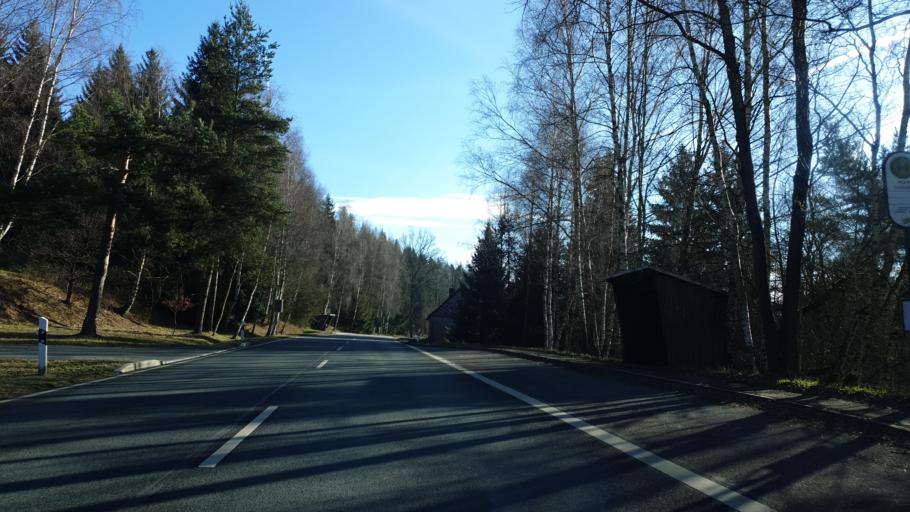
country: DE
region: Saxony
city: Markneukirchen
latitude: 50.2722
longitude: 12.2952
